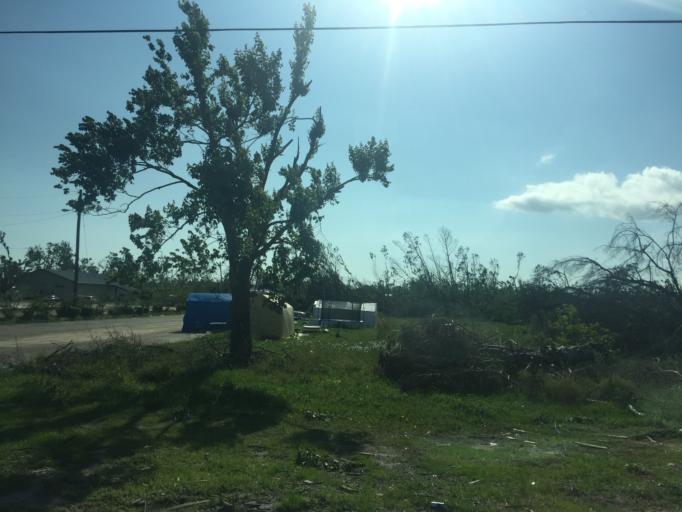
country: US
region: Florida
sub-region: Bay County
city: Springfield
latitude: 30.1613
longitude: -85.6165
